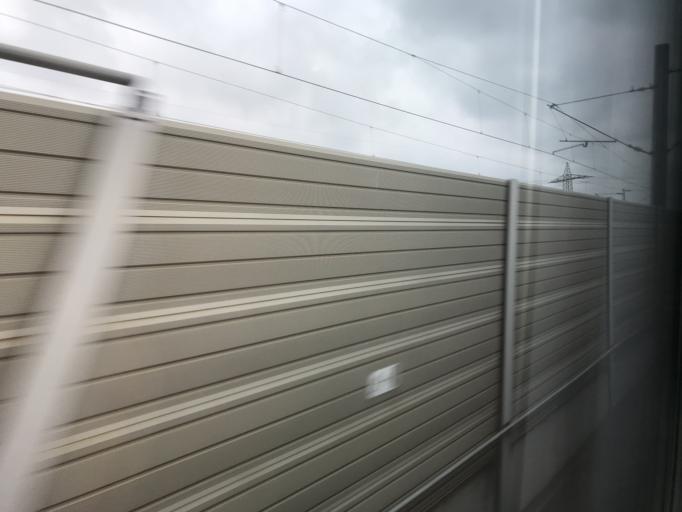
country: DE
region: Bavaria
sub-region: Upper Bavaria
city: Olching
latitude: 48.2125
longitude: 11.3177
